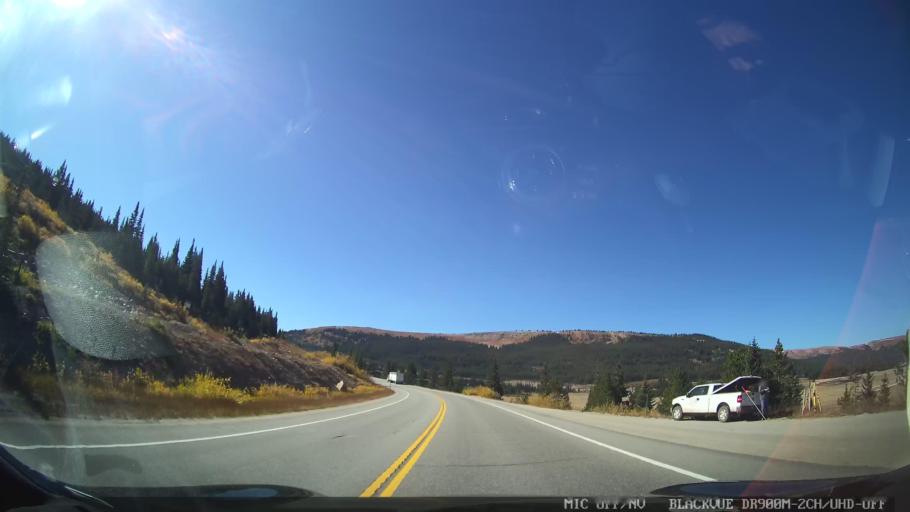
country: US
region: Colorado
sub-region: Lake County
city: Leadville
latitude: 39.3902
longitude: -106.1894
